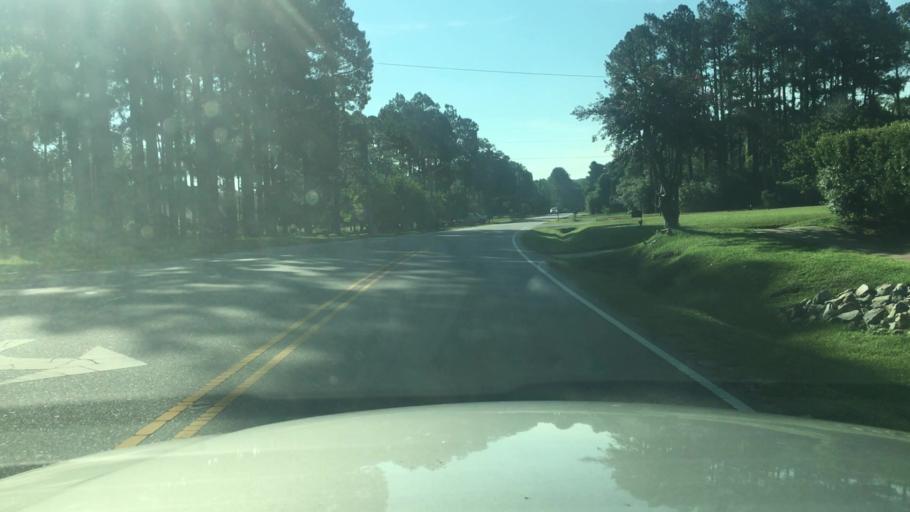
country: US
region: North Carolina
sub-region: Cumberland County
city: Fayetteville
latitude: 35.1288
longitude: -78.8944
